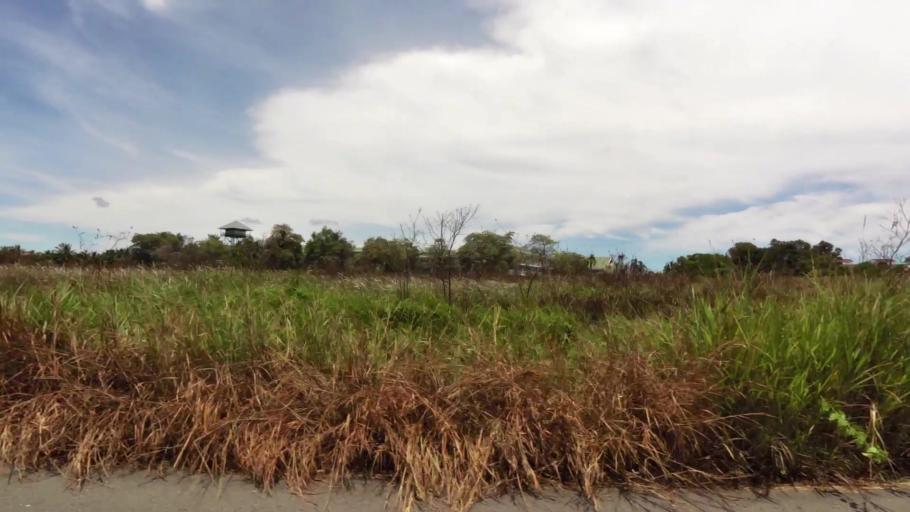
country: BN
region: Belait
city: Kuala Belait
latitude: 4.5901
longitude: 114.2441
